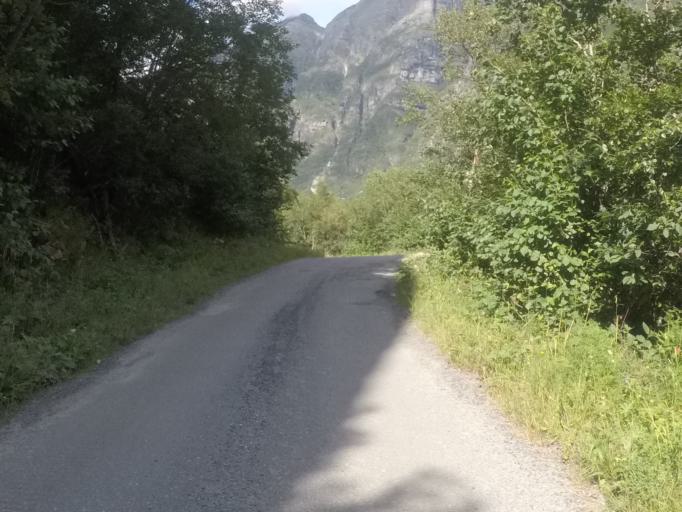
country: NO
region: Sogn og Fjordane
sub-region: Stryn
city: Stryn
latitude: 61.7520
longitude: 7.0343
